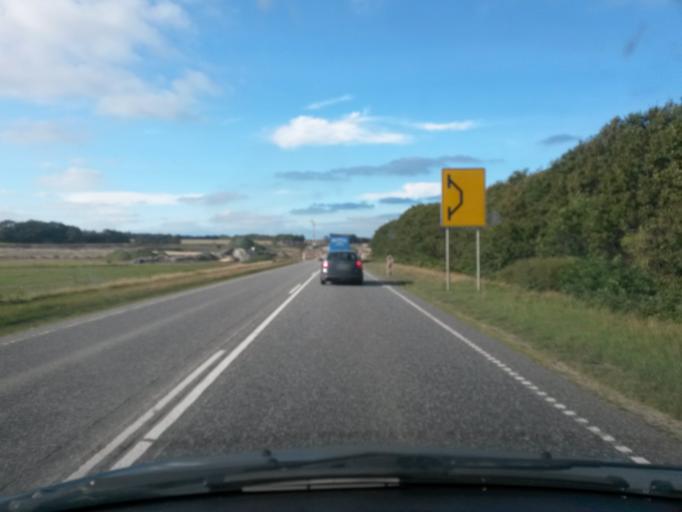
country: DK
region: Central Jutland
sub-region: Herning Kommune
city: Avlum
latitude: 56.2901
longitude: 8.7352
